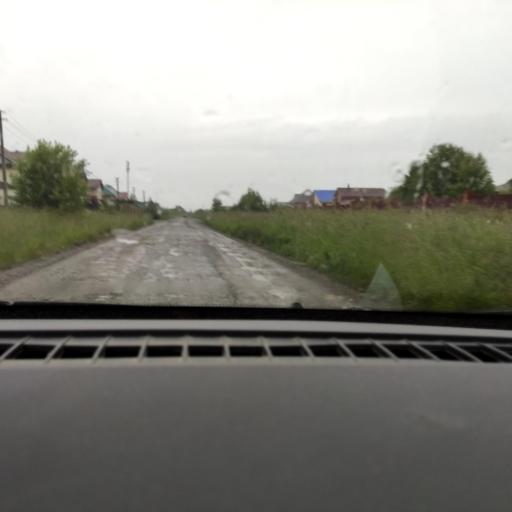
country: RU
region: Perm
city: Perm
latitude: 58.0391
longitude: 56.3723
